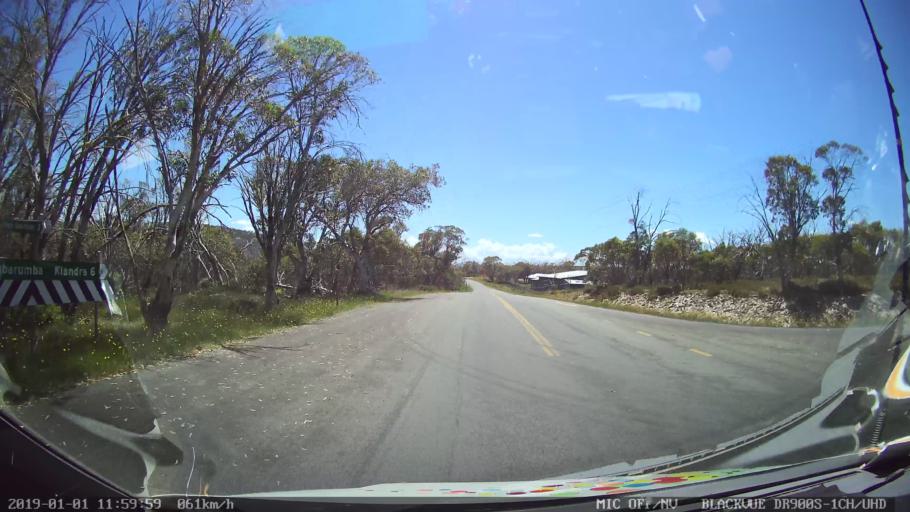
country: AU
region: New South Wales
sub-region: Snowy River
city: Jindabyne
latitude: -35.8882
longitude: 148.4562
